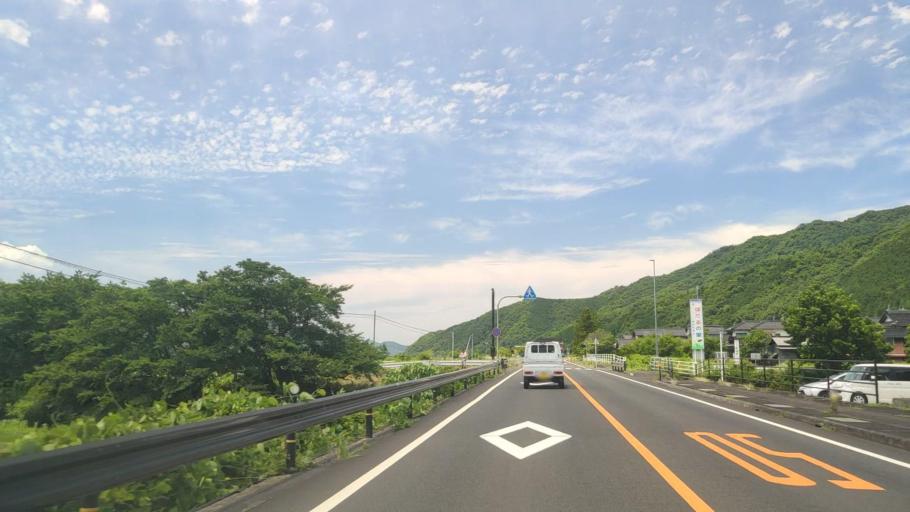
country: JP
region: Tottori
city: Tottori
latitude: 35.3696
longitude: 134.3107
